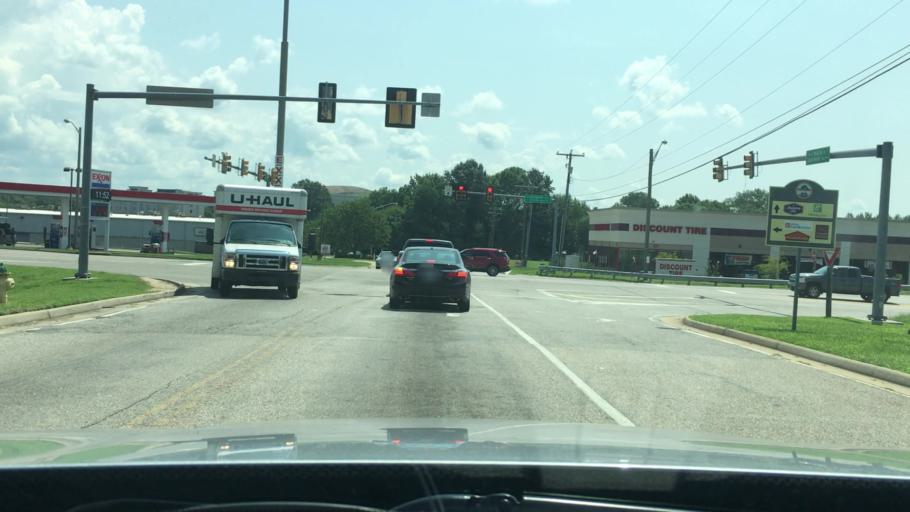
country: US
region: Virginia
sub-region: City of Petersburg
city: Petersburg
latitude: 37.2424
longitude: -77.3921
